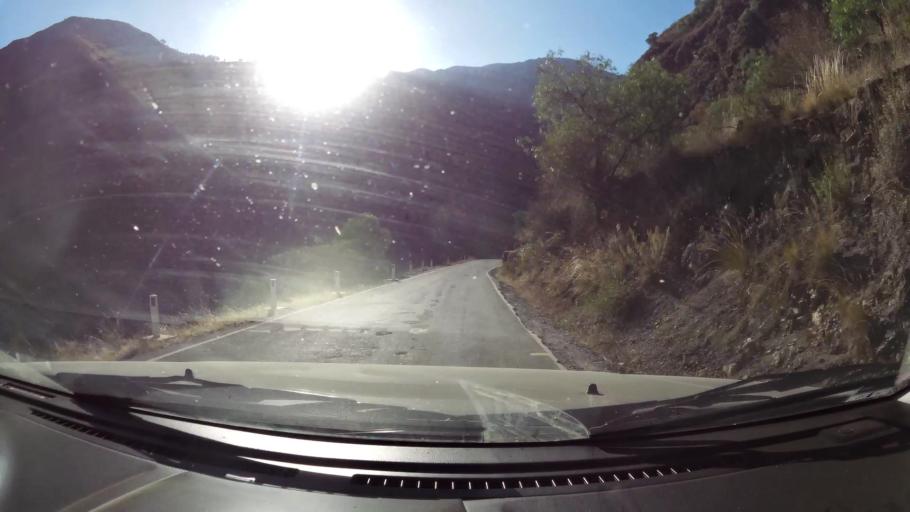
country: PE
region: Huancavelica
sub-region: Provincia de Churcampa
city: La Esmeralda
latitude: -12.5625
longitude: -74.7067
